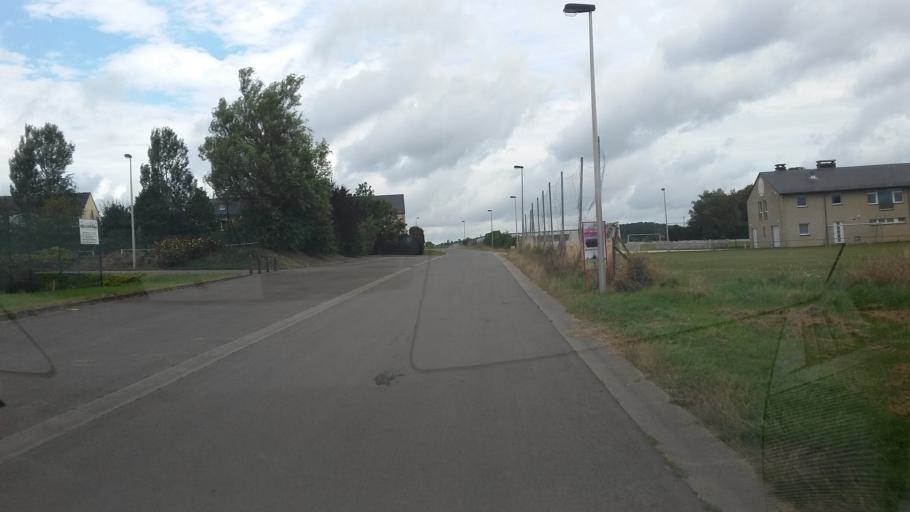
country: BE
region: Wallonia
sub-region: Province du Luxembourg
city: Arlon
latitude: 49.6752
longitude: 5.8466
